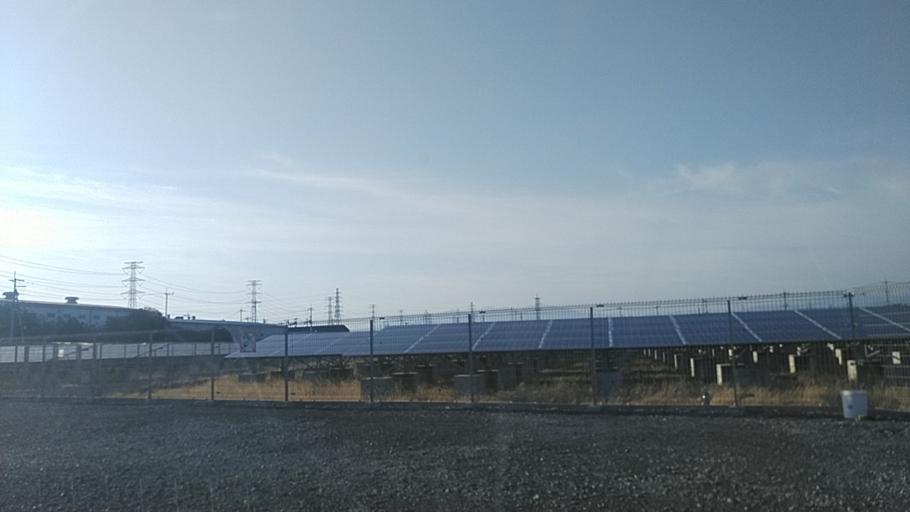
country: JP
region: Gunma
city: Ota
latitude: 36.2771
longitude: 139.3426
